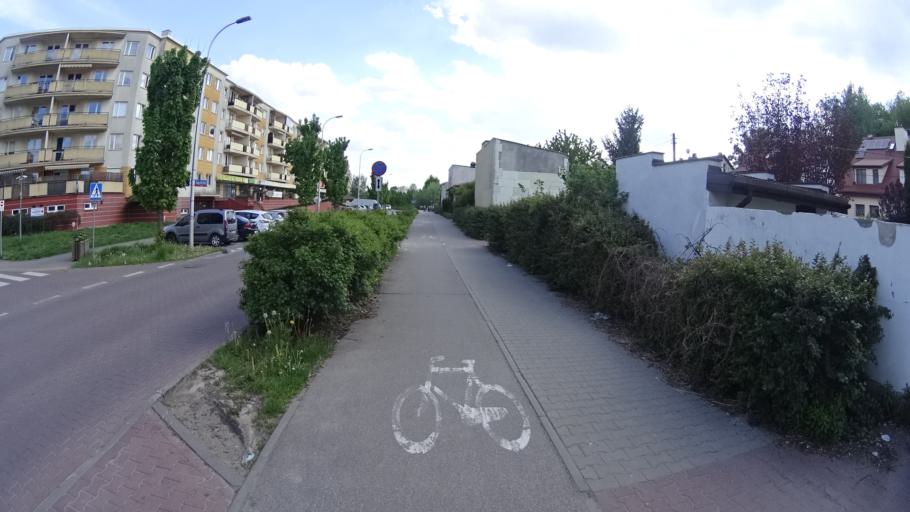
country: PL
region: Masovian Voivodeship
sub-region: Warszawa
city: Mokotow
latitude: 52.2115
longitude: 21.0587
